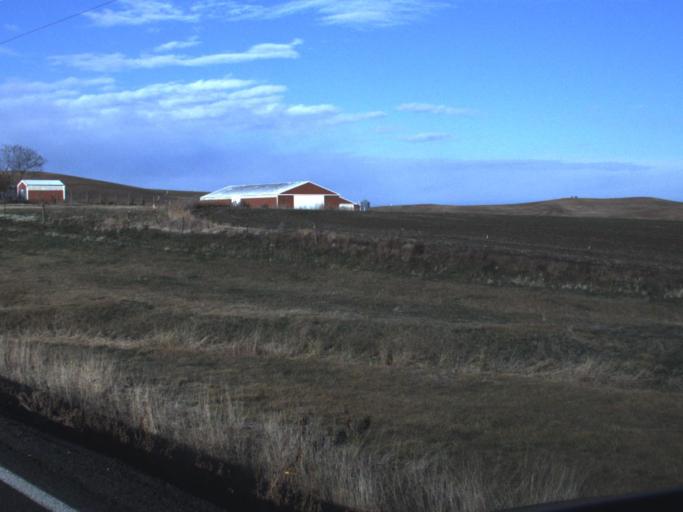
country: US
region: Washington
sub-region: Whitman County
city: Pullman
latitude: 46.7250
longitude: -117.2382
